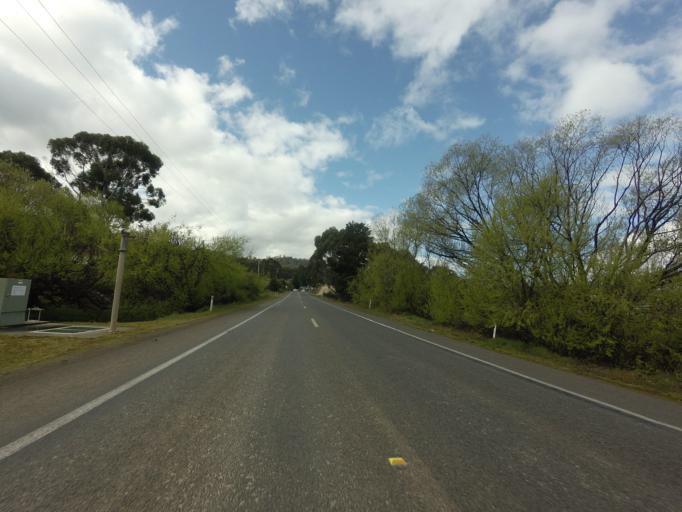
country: AU
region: Tasmania
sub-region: Huon Valley
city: Geeveston
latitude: -43.1575
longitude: 146.9552
